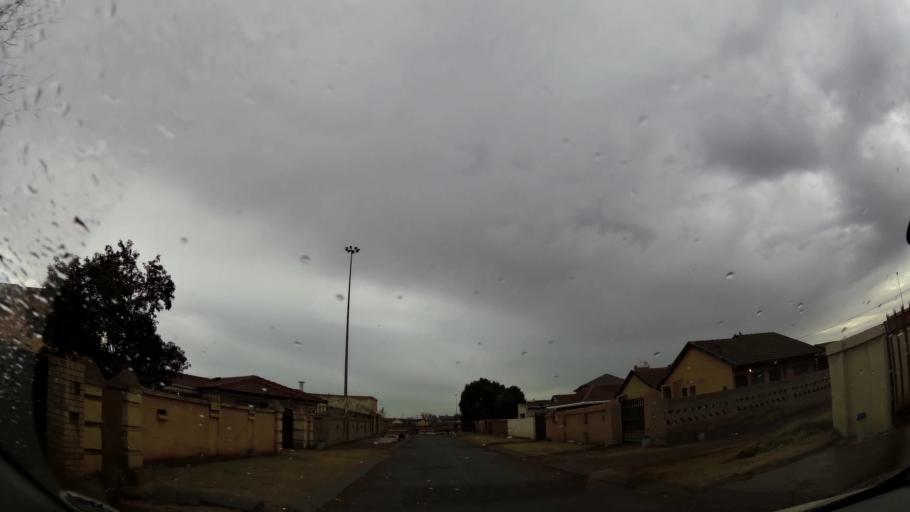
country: ZA
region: Gauteng
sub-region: Ekurhuleni Metropolitan Municipality
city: Germiston
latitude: -26.3366
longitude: 28.2023
